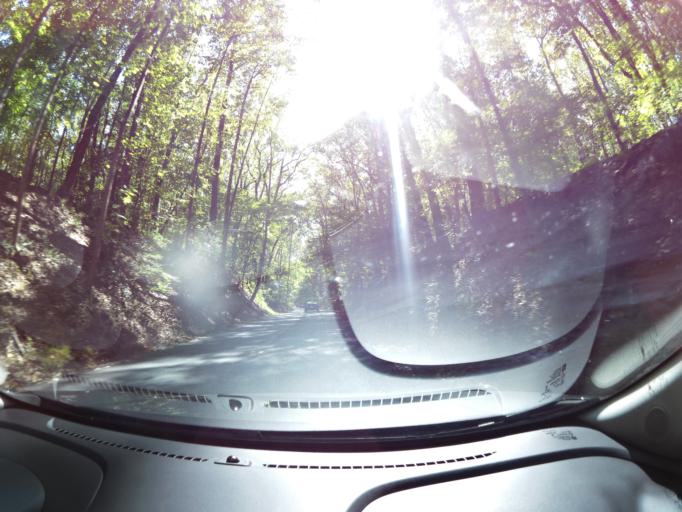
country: US
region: Virginia
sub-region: Fairfax County
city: Great Falls
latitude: 38.9859
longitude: -77.2562
